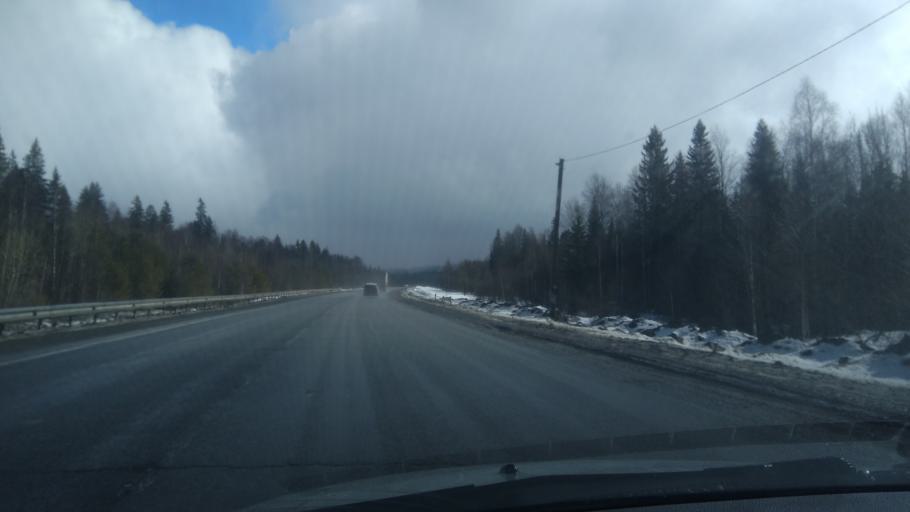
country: RU
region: Sverdlovsk
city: Arti
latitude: 56.7940
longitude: 58.4879
